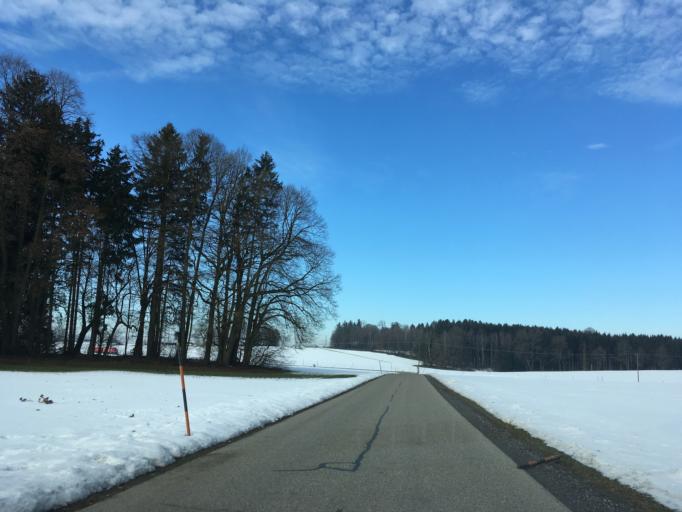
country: DE
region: Bavaria
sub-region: Upper Bavaria
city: Stephanskirchen
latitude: 47.8780
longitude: 12.1618
